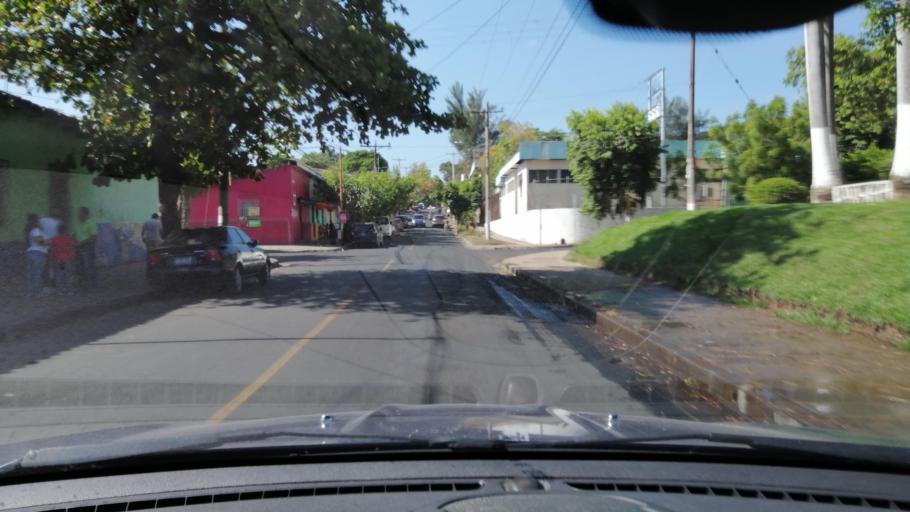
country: SV
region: Santa Ana
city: Santa Ana
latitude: 13.9935
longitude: -89.5500
